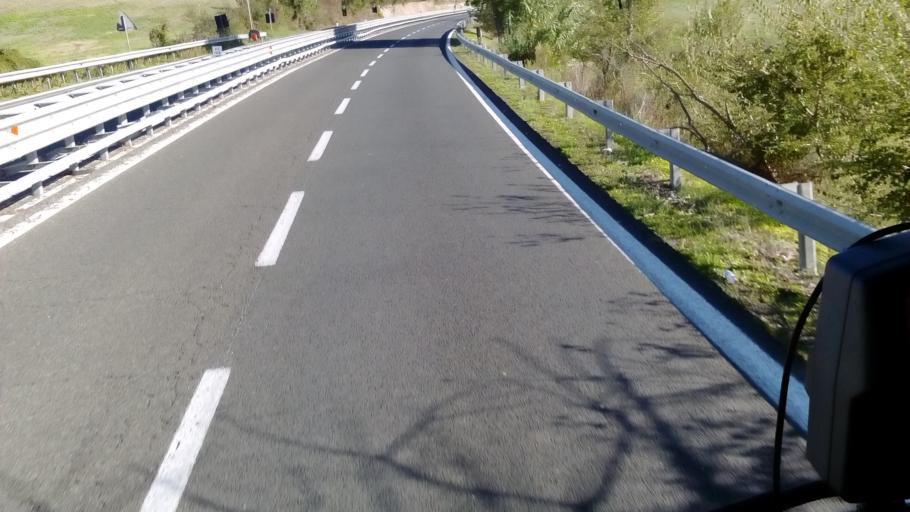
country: IT
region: Latium
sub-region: Provincia di Viterbo
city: Montalto di Castro
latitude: 42.3204
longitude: 11.6479
